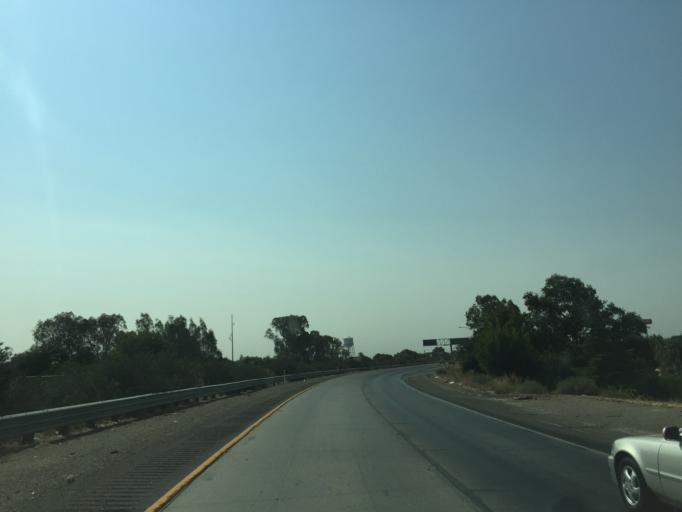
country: US
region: California
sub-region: Merced County
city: Merced
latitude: 37.2953
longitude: -120.4781
